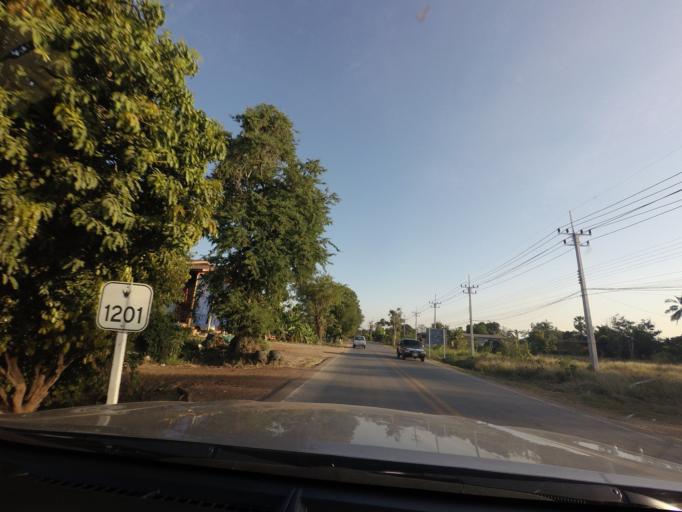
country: TH
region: Sukhothai
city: Sawankhalok
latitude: 17.3673
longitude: 99.8044
